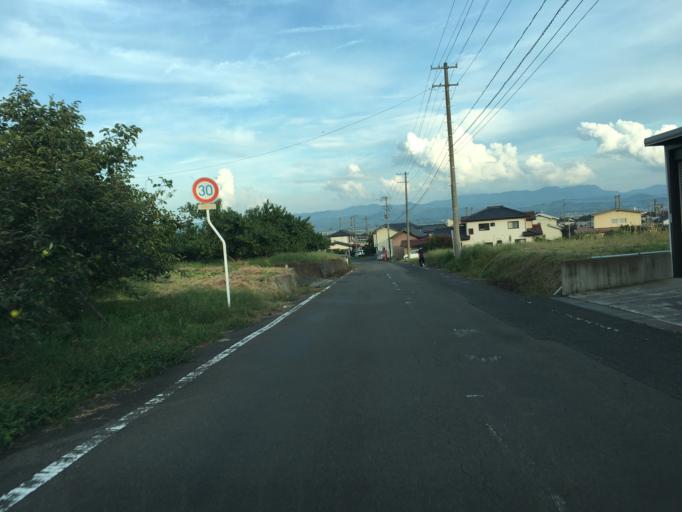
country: JP
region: Fukushima
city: Hobaramachi
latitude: 37.8585
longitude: 140.5172
